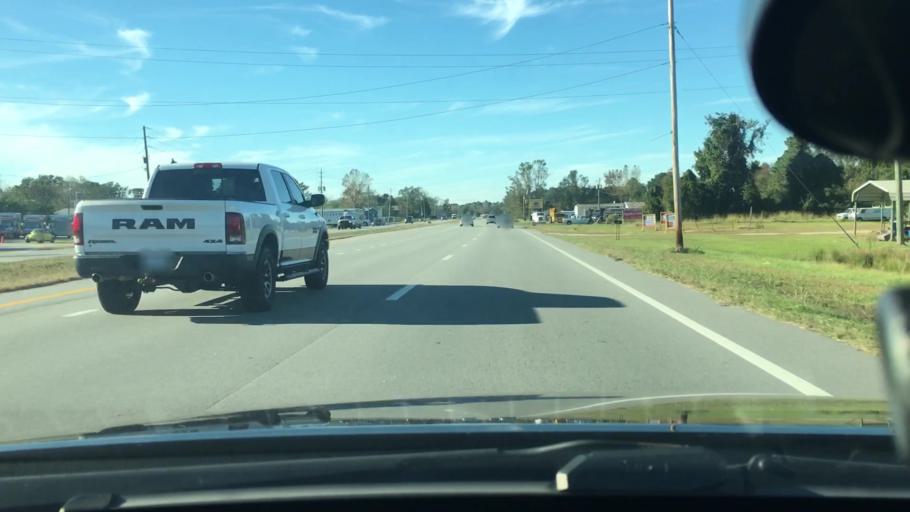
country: US
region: North Carolina
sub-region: Craven County
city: New Bern
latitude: 35.1211
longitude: -77.0181
